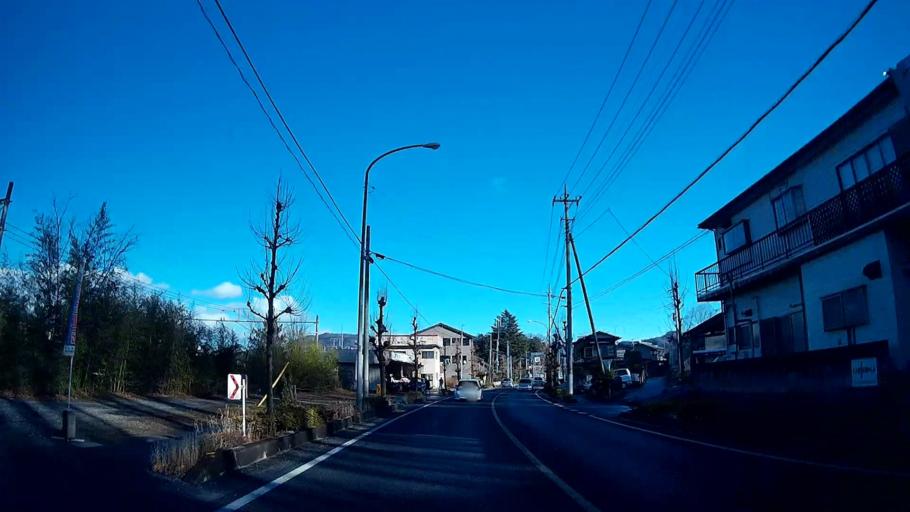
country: JP
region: Saitama
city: Chichibu
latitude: 36.0177
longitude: 139.0935
